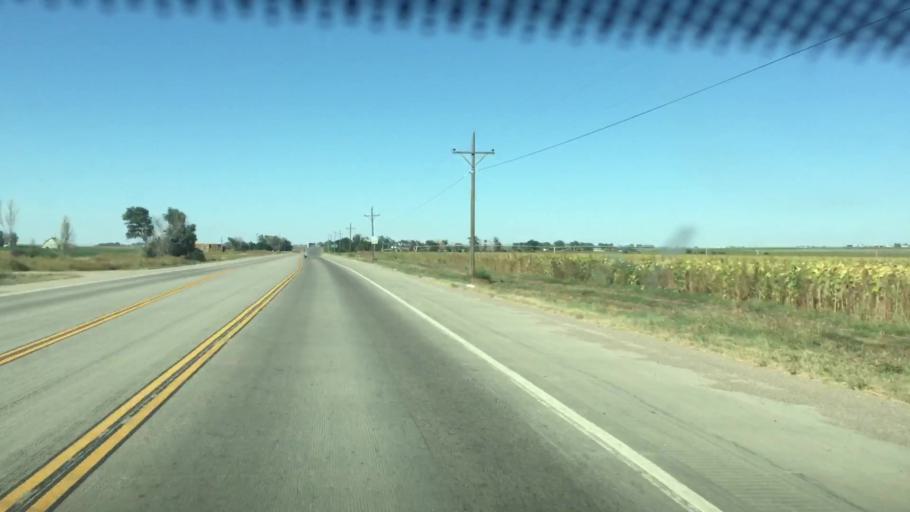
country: US
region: Colorado
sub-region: Prowers County
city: Lamar
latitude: 38.1598
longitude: -102.7237
